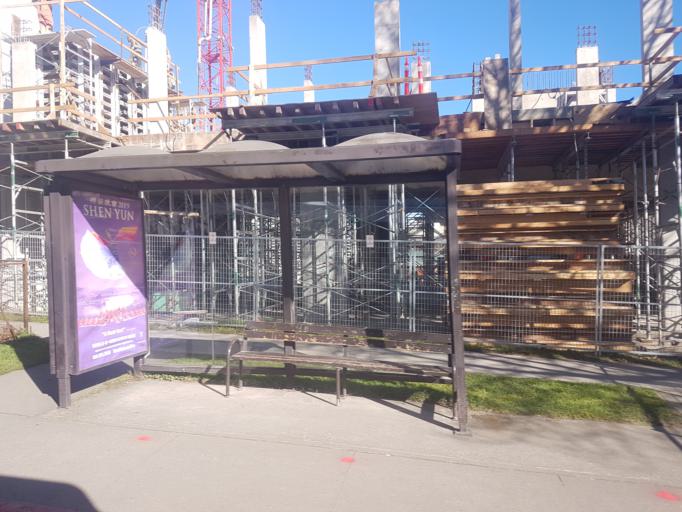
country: CA
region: British Columbia
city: Victoria
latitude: 48.4262
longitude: -123.3533
